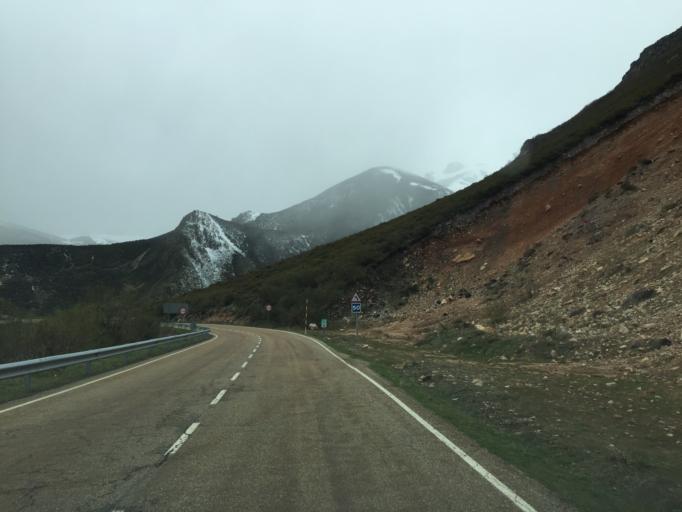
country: ES
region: Castille and Leon
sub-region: Provincia de Leon
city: San Emiliano
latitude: 43.0344
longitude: -6.0159
